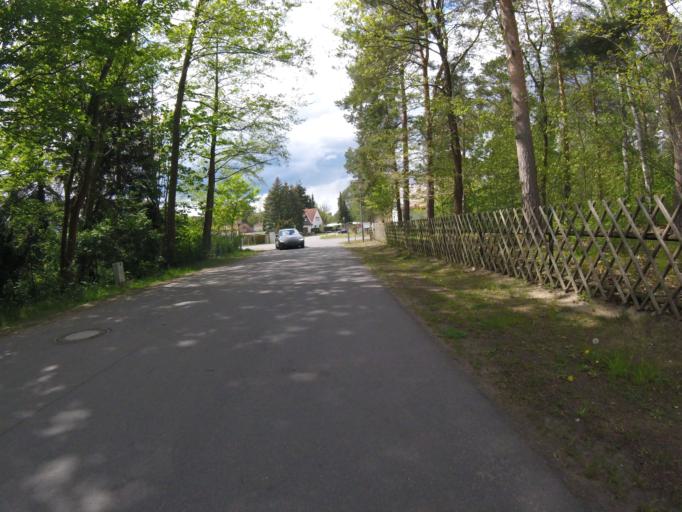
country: DE
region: Brandenburg
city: Schwerin
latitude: 52.1583
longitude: 13.6334
